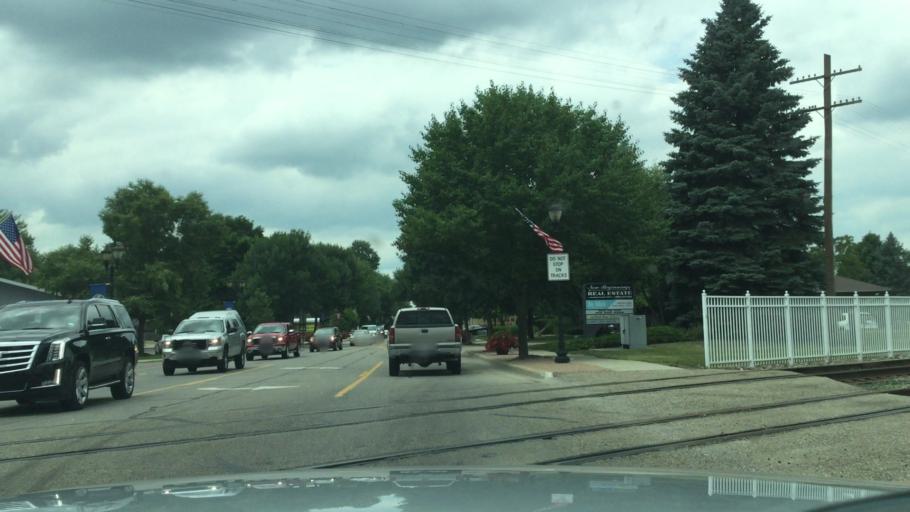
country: US
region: Michigan
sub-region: Saginaw County
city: Birch Run
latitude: 43.2502
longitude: -83.7938
